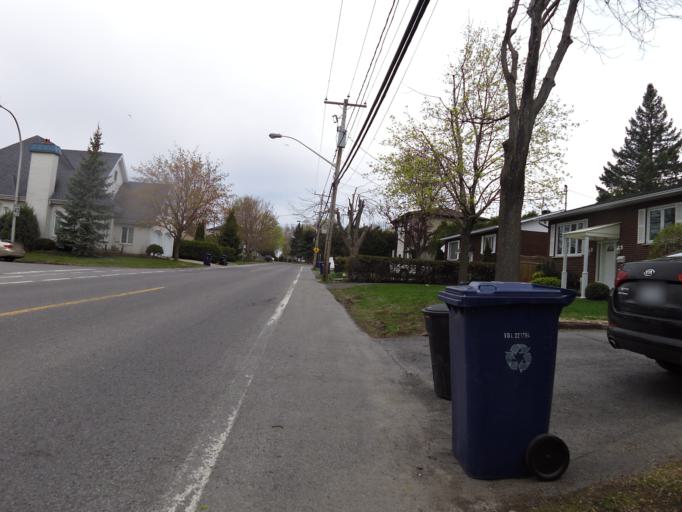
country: CA
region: Quebec
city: Dollard-Des Ormeaux
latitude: 45.5207
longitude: -73.8232
